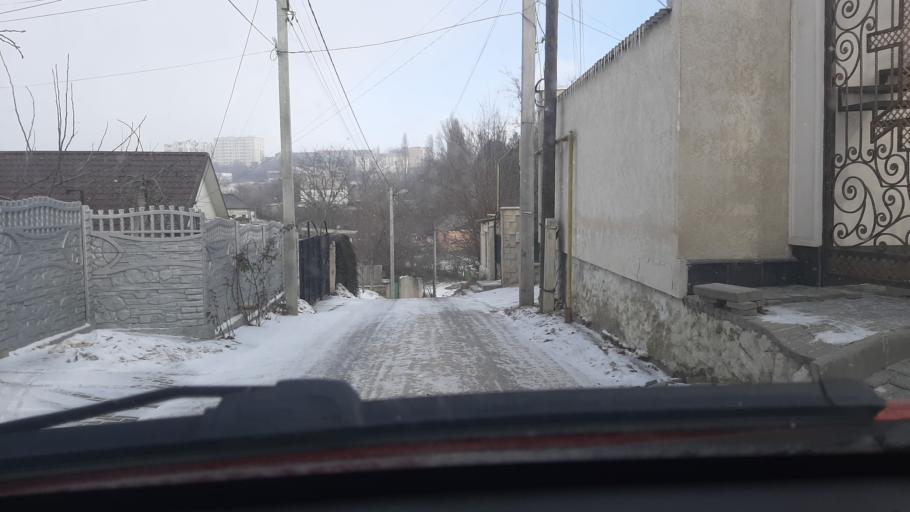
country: MD
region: Laloveni
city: Ialoveni
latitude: 46.9945
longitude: 28.7787
